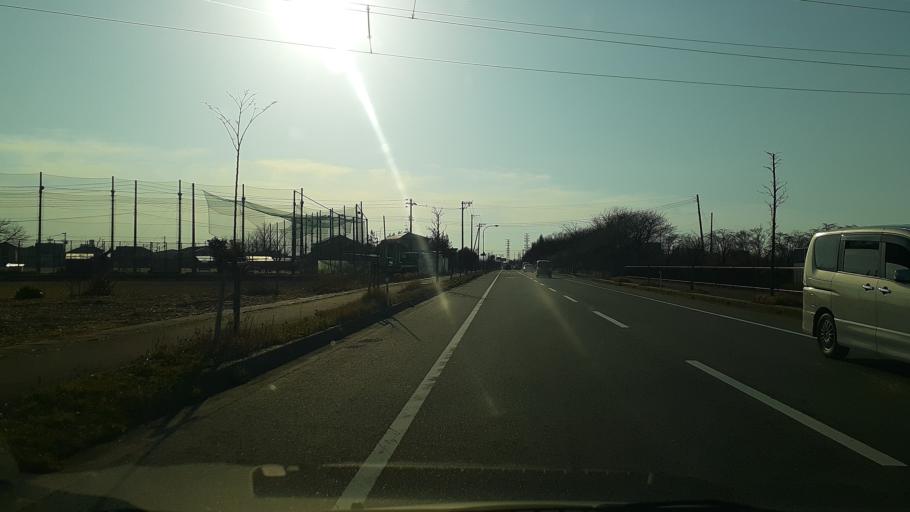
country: JP
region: Niigata
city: Niitsu-honcho
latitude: 37.8064
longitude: 139.1414
